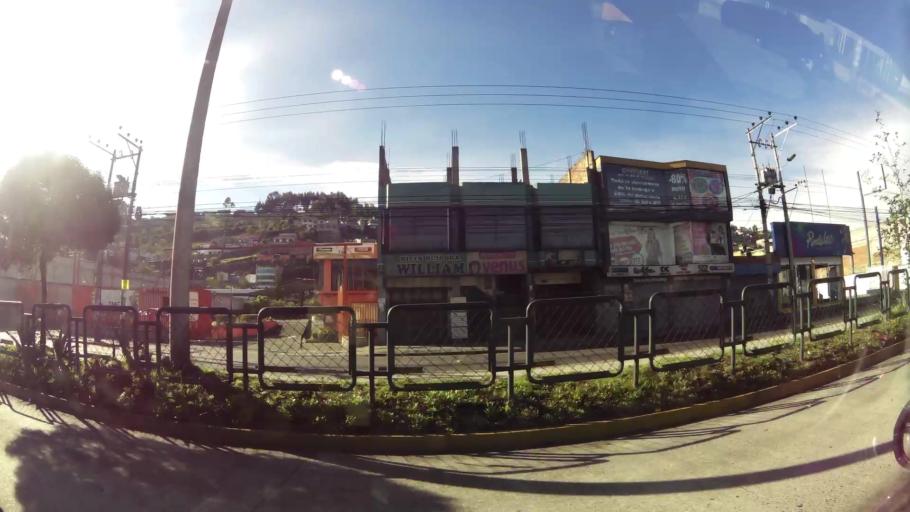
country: EC
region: Pichincha
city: Quito
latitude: -0.2805
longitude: -78.5334
